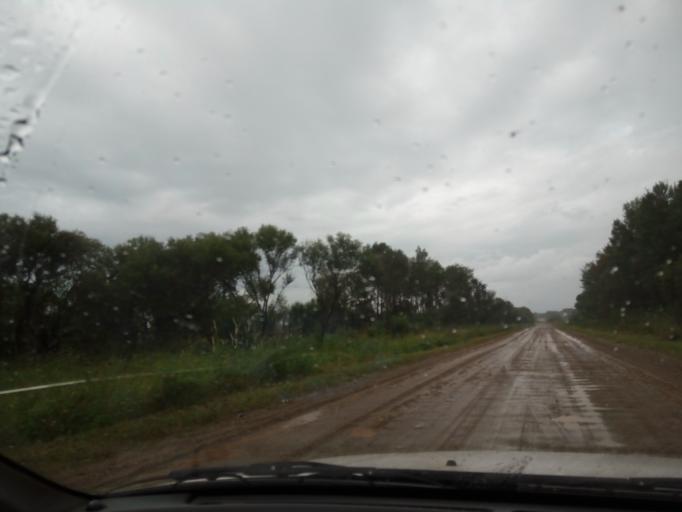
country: RU
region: Primorskiy
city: Lazo
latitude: 45.8479
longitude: 133.6453
